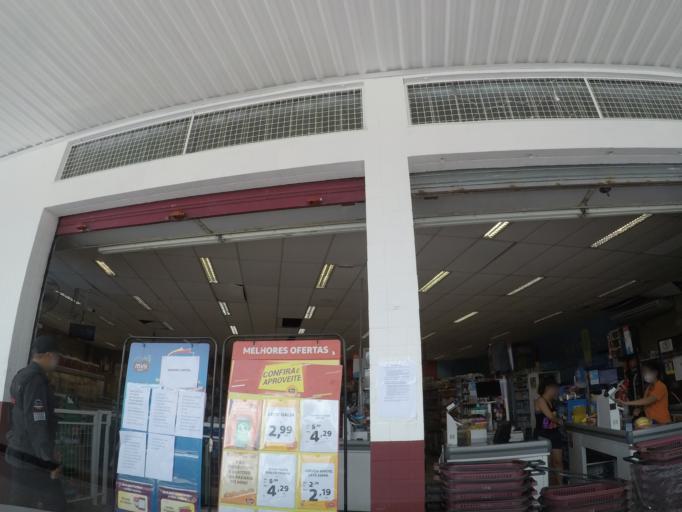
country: BR
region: Sao Paulo
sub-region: Mongagua
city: Mongagua
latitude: -24.0611
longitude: -46.5588
